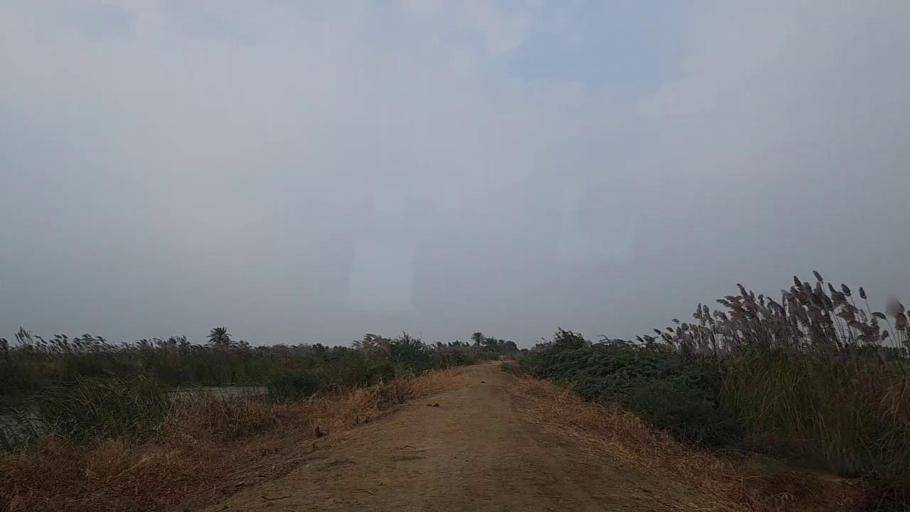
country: PK
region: Sindh
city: Gharo
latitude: 24.6258
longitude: 67.5029
